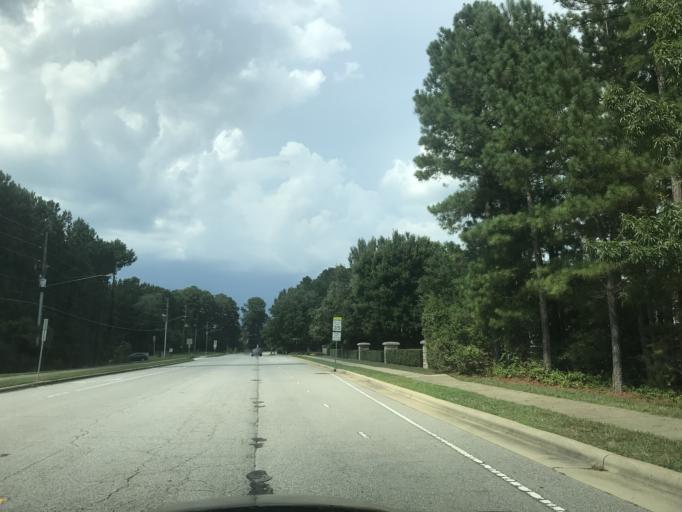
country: US
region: North Carolina
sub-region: Wake County
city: West Raleigh
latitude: 35.8902
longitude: -78.6557
